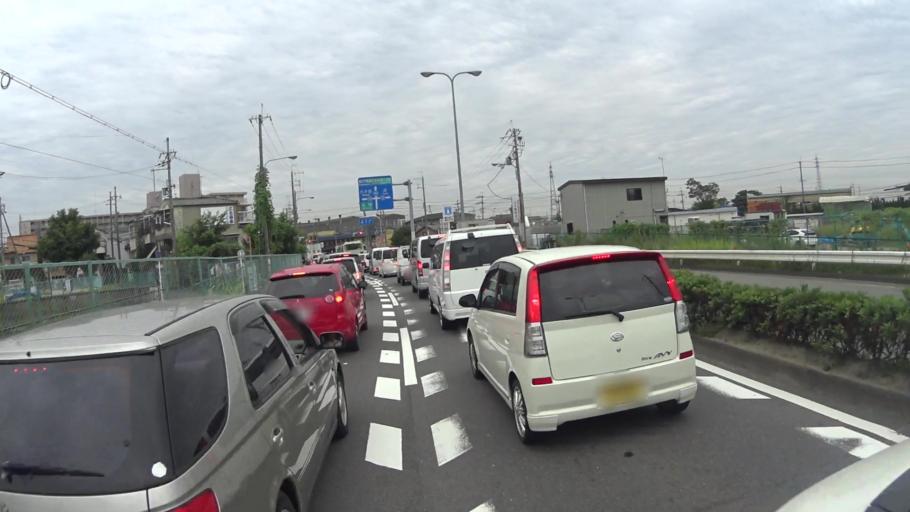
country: JP
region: Kyoto
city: Muko
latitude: 34.9283
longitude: 135.7385
